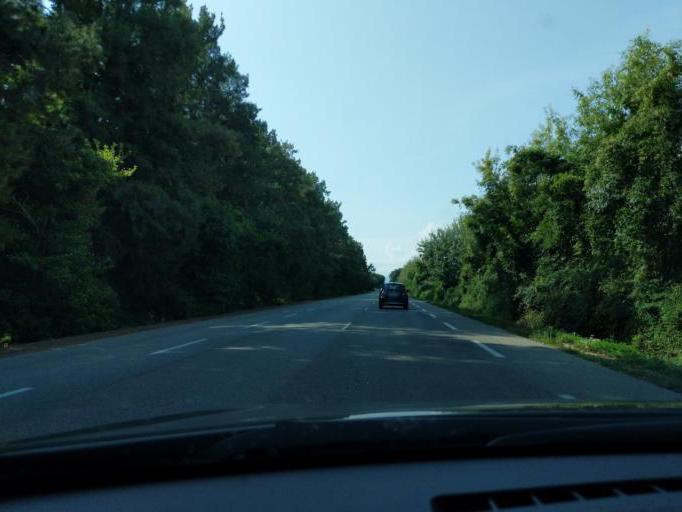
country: FR
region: Corsica
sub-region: Departement de la Haute-Corse
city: Ghisonaccia
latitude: 41.9716
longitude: 9.3987
